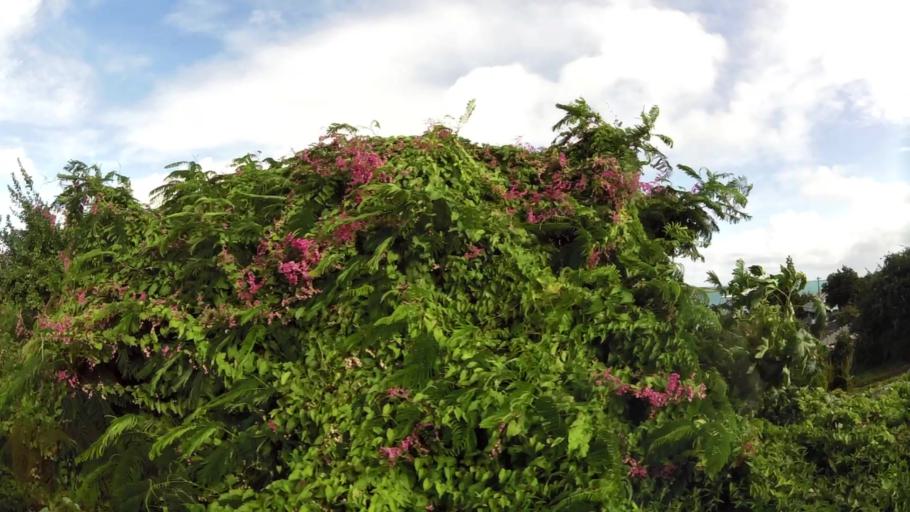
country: AG
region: Saint Peter
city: Parham
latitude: 17.0953
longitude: -61.7244
